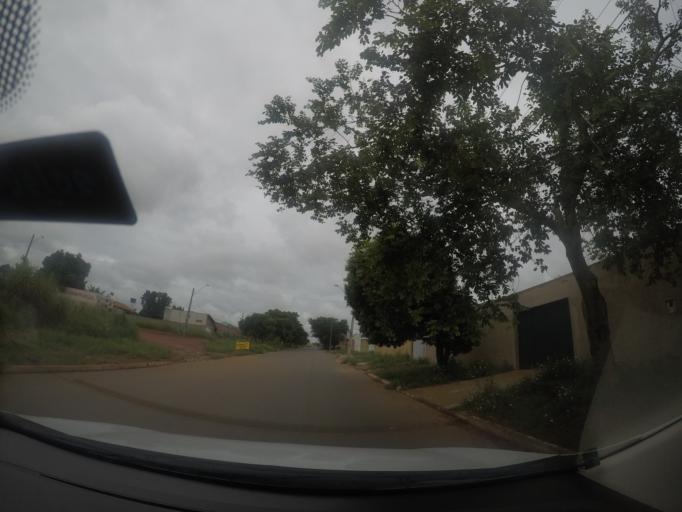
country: BR
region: Goias
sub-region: Trindade
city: Trindade
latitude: -16.6855
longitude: -49.4035
